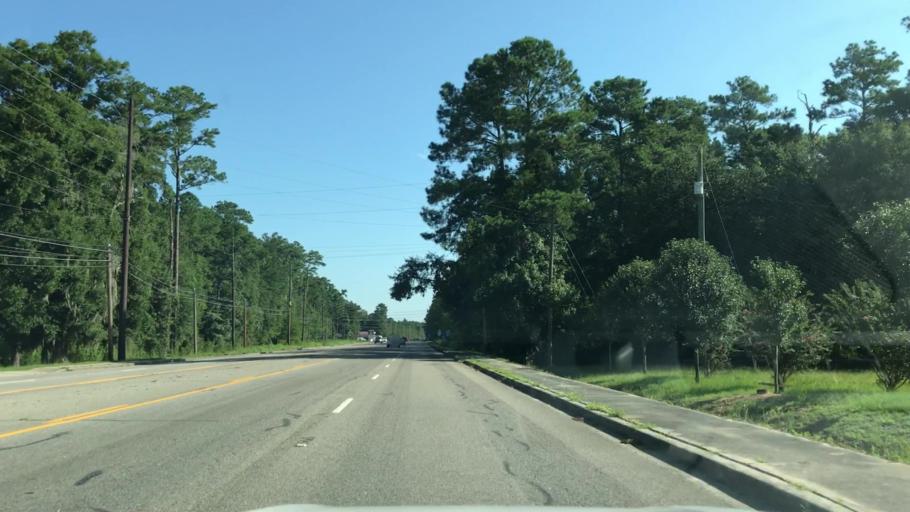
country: US
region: South Carolina
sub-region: Georgetown County
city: Georgetown
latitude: 33.4129
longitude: -79.2852
